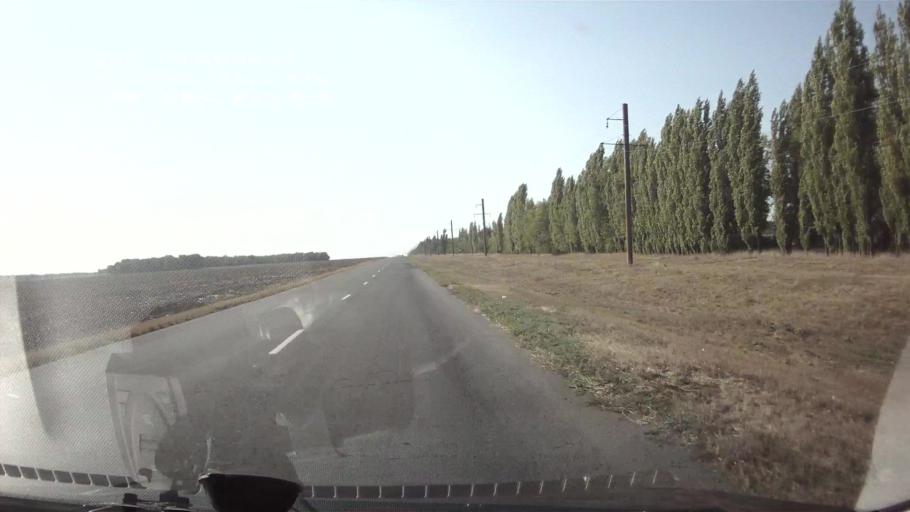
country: RU
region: Rostov
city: Tselina
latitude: 46.5333
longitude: 40.8998
